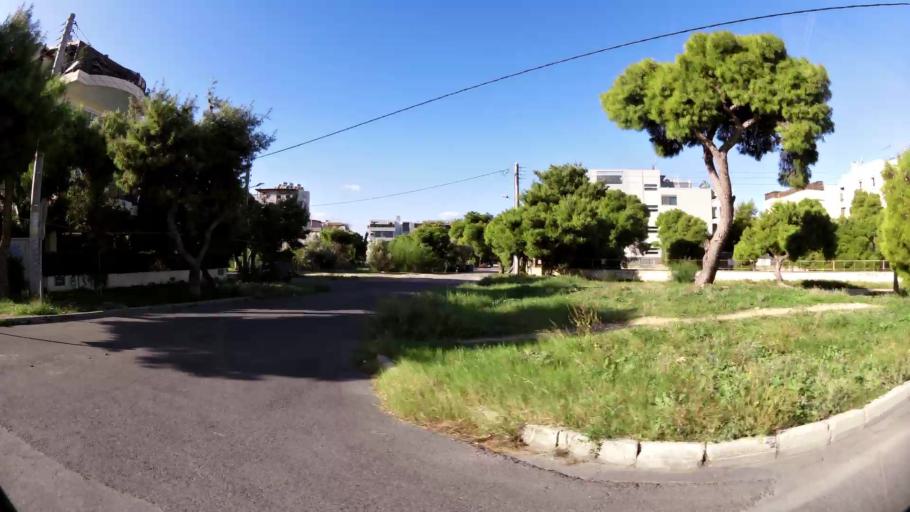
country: GR
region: Attica
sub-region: Nomarchia Athinas
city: Elliniko
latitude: 37.8712
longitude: 23.7406
